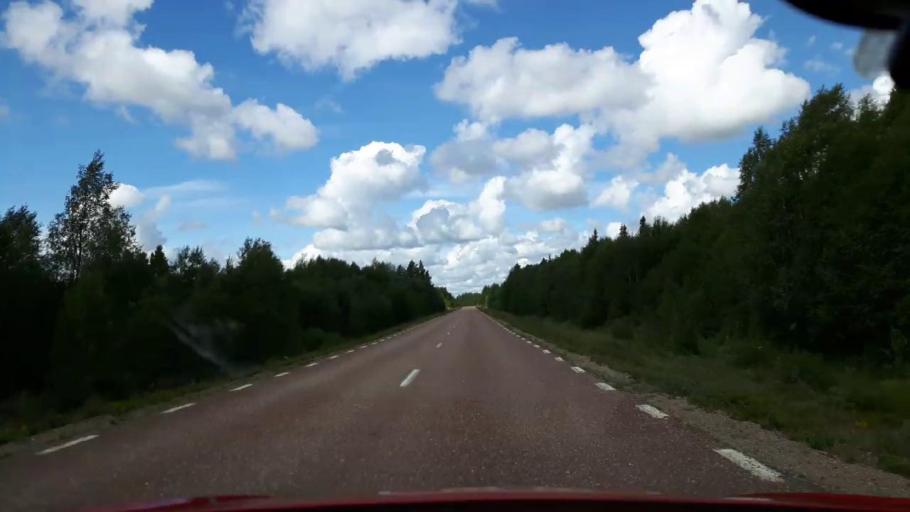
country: SE
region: Dalarna
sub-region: Alvdalens Kommun
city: AElvdalen
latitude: 61.8013
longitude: 13.6653
